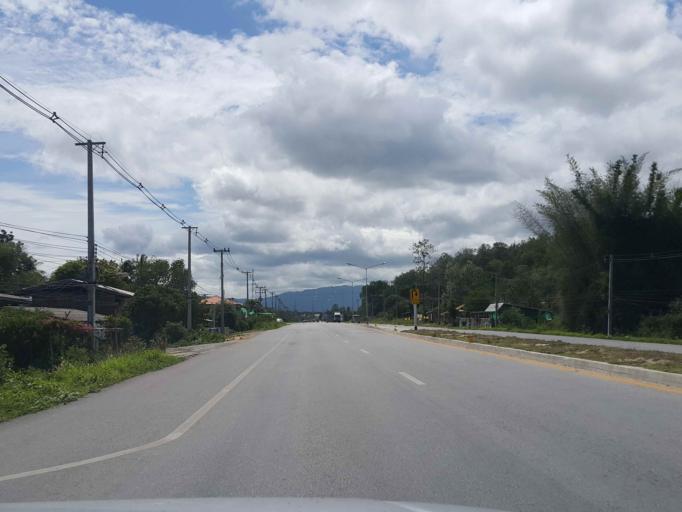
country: TH
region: Tak
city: Tak
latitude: 16.8869
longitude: 99.1779
